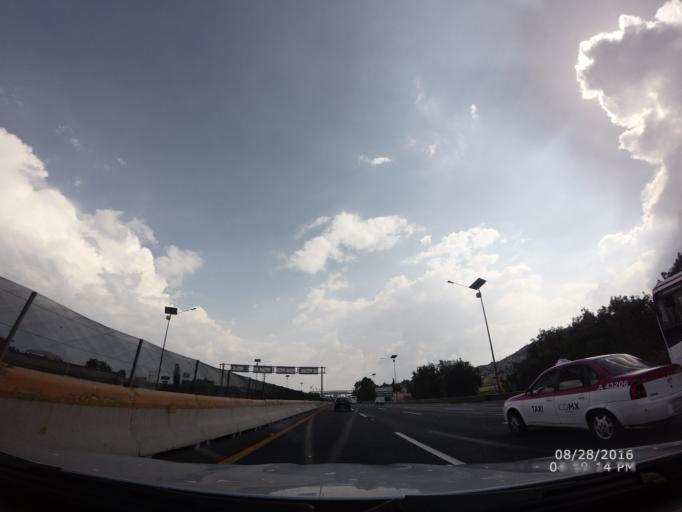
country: MX
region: Mexico
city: Ecatepec
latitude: 19.5938
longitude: -99.0406
